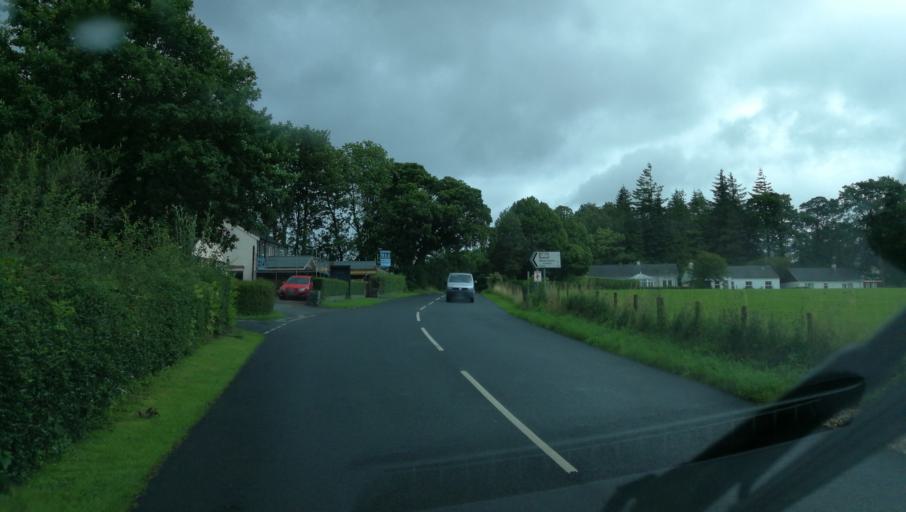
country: GB
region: England
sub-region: Cumbria
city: Penrith
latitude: 54.5836
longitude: -2.8738
